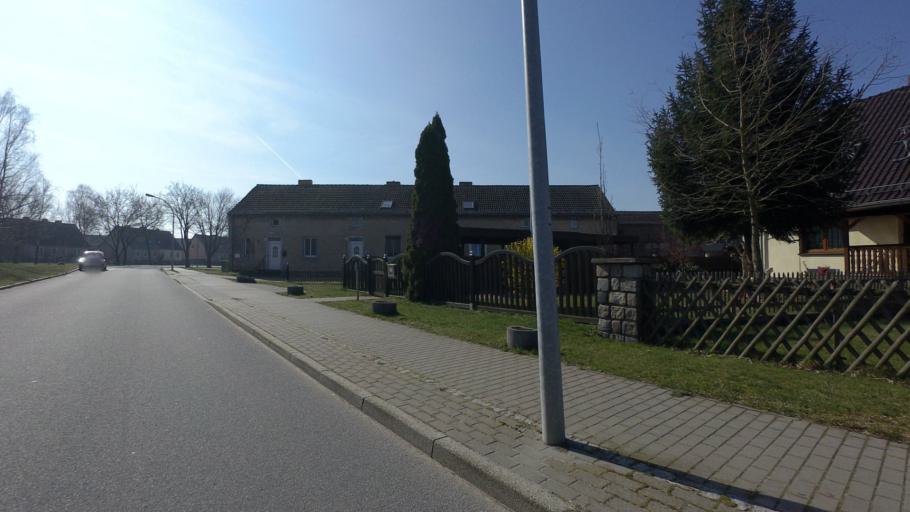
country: DE
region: Brandenburg
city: Schonefeld
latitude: 52.3551
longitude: 13.4713
